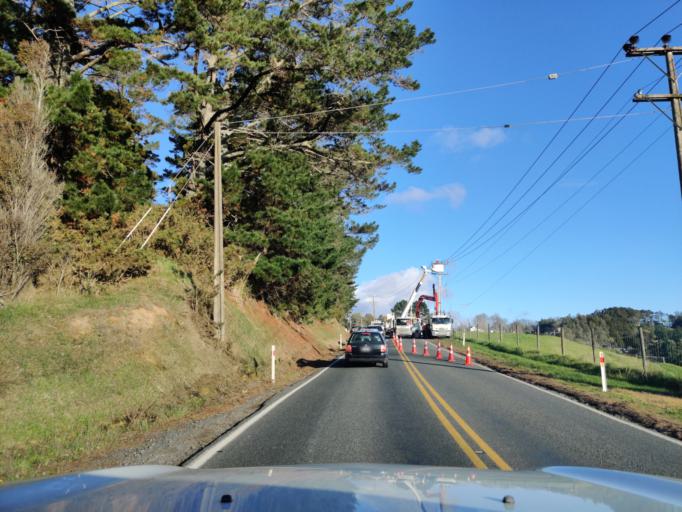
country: NZ
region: Auckland
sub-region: Auckland
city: Red Hill
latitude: -36.9691
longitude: 174.9851
